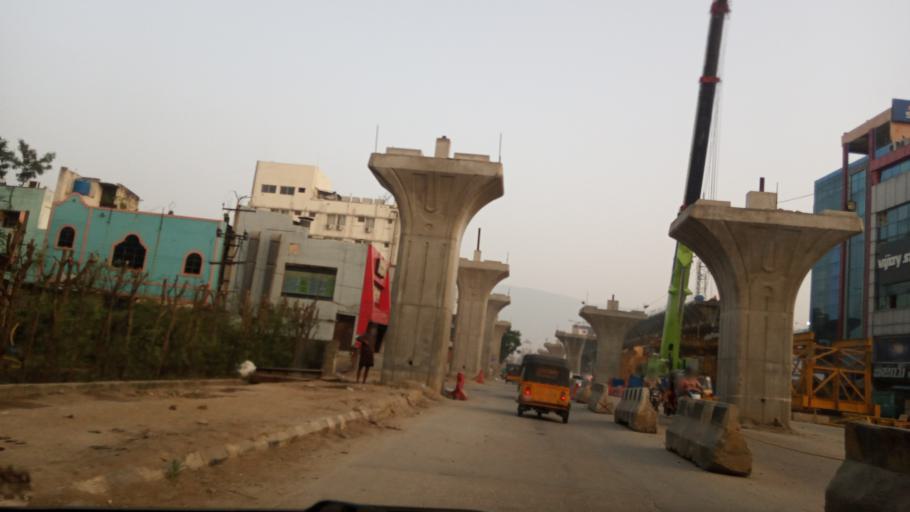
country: IN
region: Andhra Pradesh
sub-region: Chittoor
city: Tirupati
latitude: 13.6338
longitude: 79.4278
